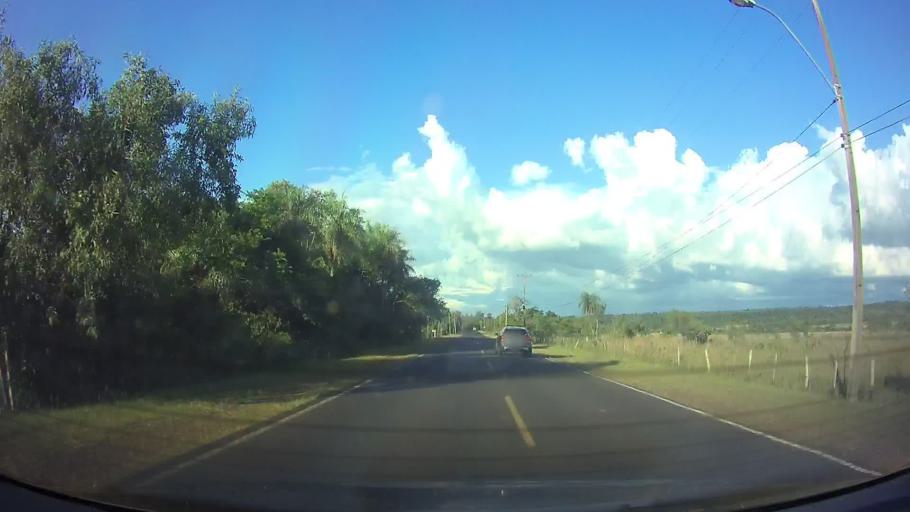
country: PY
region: Cordillera
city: Emboscada
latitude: -25.1632
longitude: -57.2674
